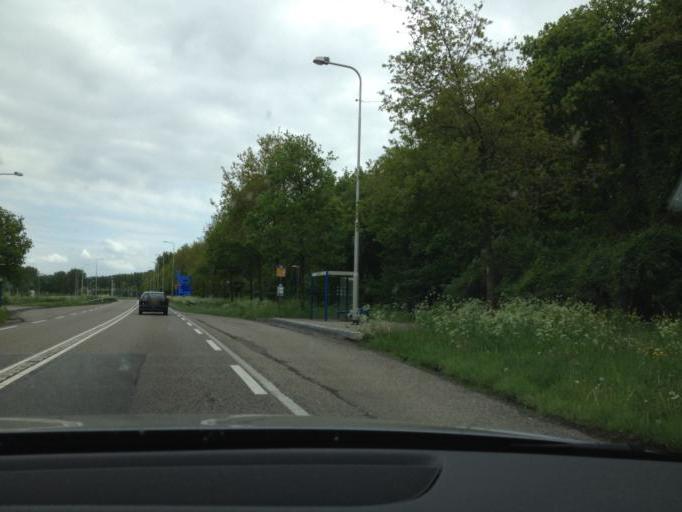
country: NL
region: North Holland
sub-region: Gemeente Huizen
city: Huizen
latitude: 52.3424
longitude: 5.2640
